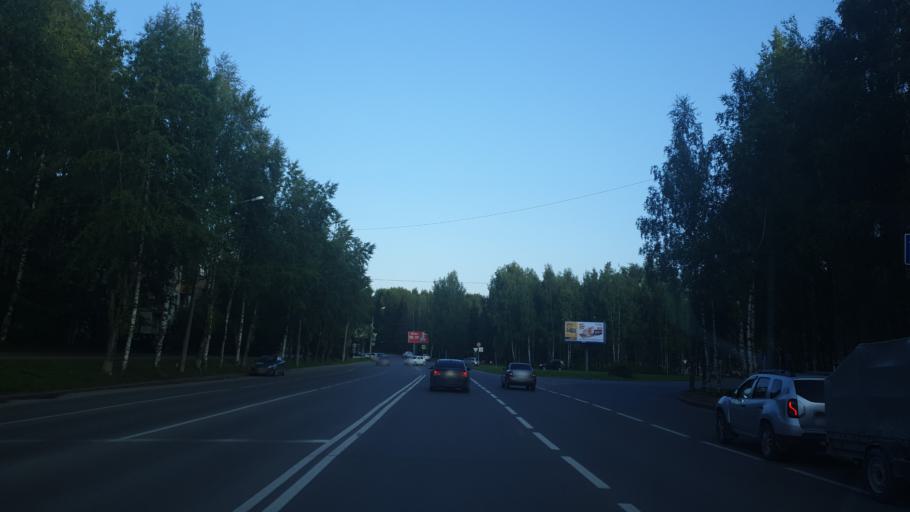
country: RU
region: Komi Republic
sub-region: Syktyvdinskiy Rayon
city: Syktyvkar
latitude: 61.6615
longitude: 50.8184
